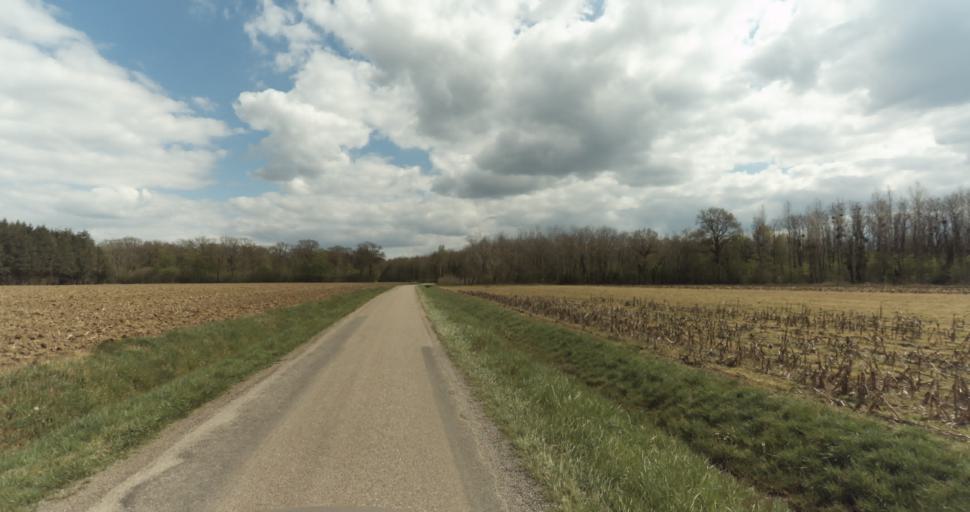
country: FR
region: Bourgogne
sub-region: Departement de la Cote-d'Or
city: Auxonne
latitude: 47.1723
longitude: 5.4199
